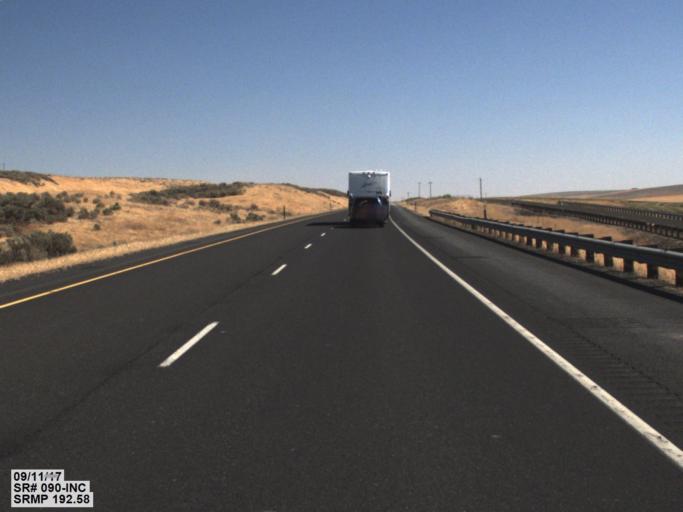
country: US
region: Washington
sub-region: Grant County
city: Warden
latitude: 47.0844
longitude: -118.9666
